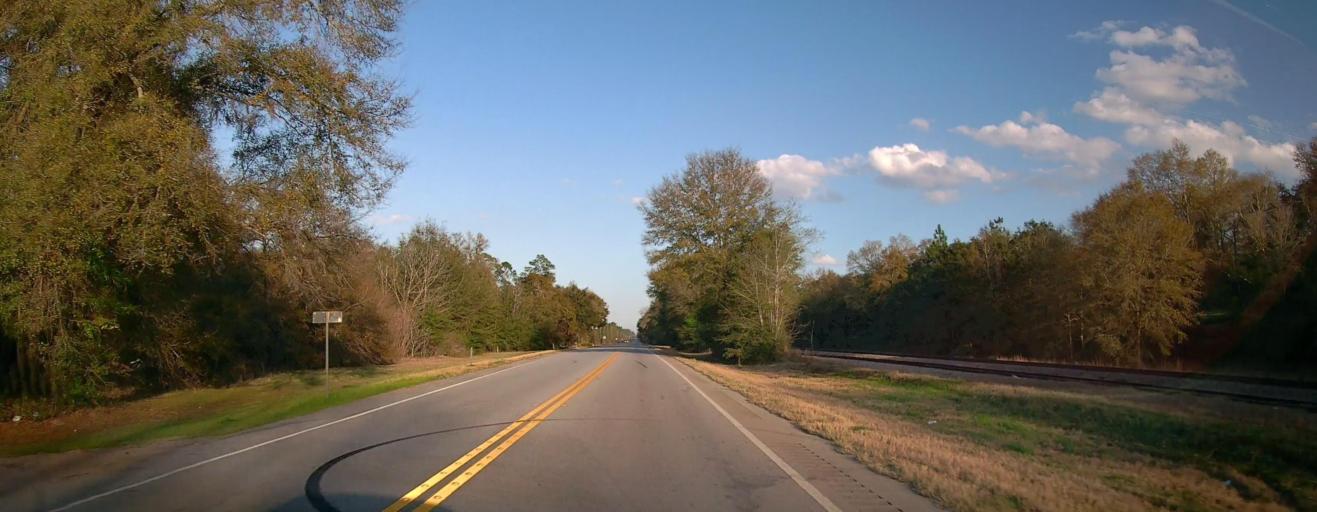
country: US
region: Georgia
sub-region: Bryan County
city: Pembroke
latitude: 32.1442
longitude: -81.7438
